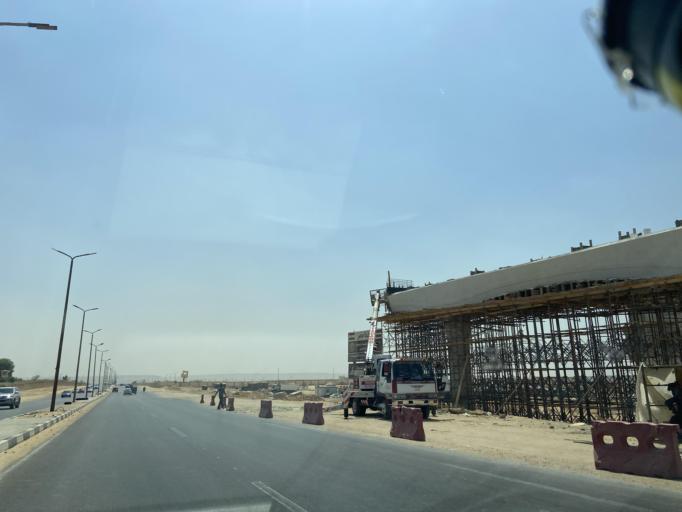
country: EG
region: Muhafazat al Qahirah
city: Cairo
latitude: 30.0027
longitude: 31.3513
